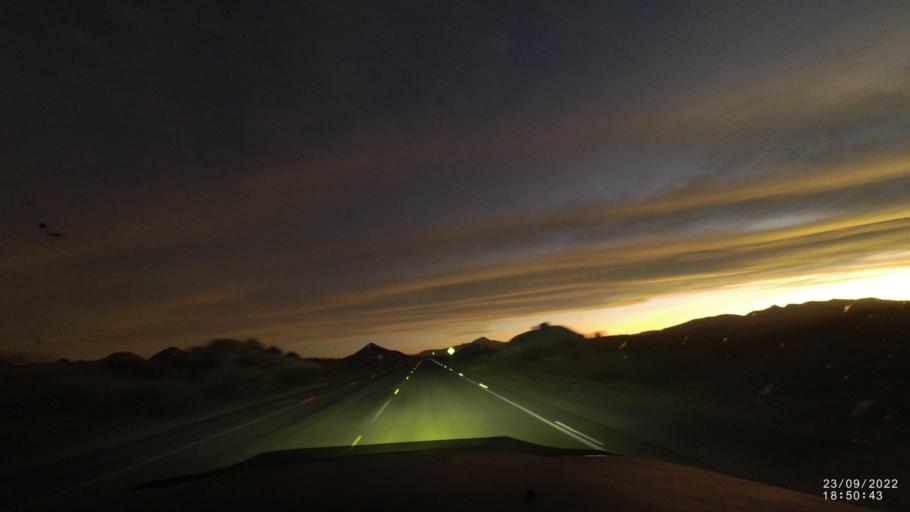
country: BO
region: Oruro
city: Challapata
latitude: -19.4669
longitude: -67.4270
